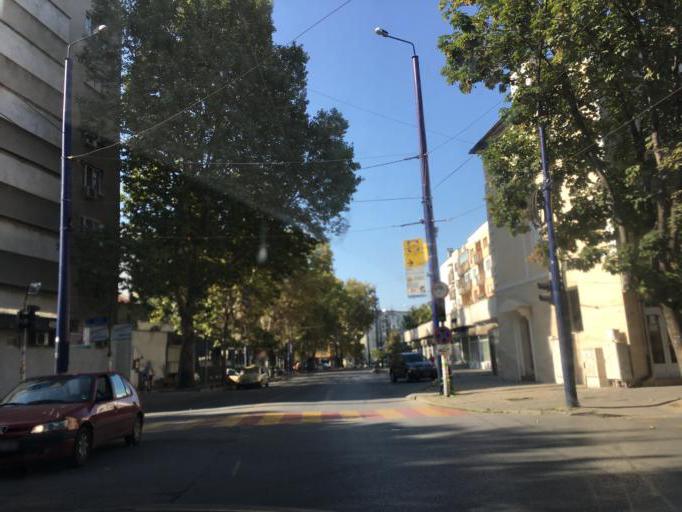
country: BG
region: Pazardzhik
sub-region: Obshtina Pazardzhik
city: Pazardzhik
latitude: 42.1936
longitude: 24.3328
